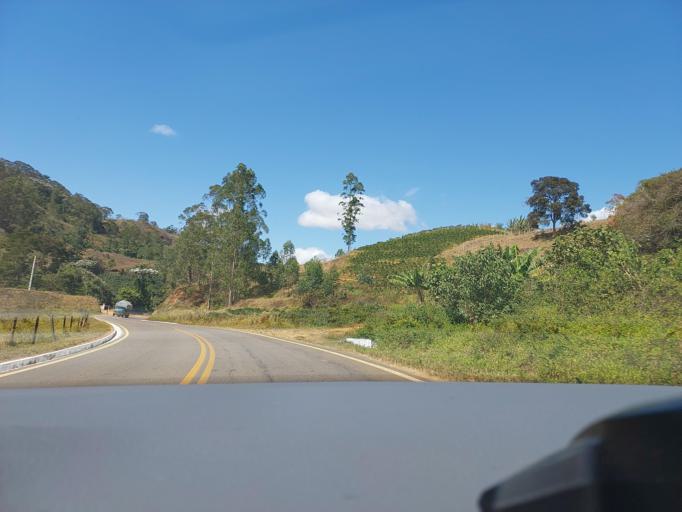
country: BR
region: Minas Gerais
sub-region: Mirai
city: Mirai
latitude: -21.0199
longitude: -42.5428
